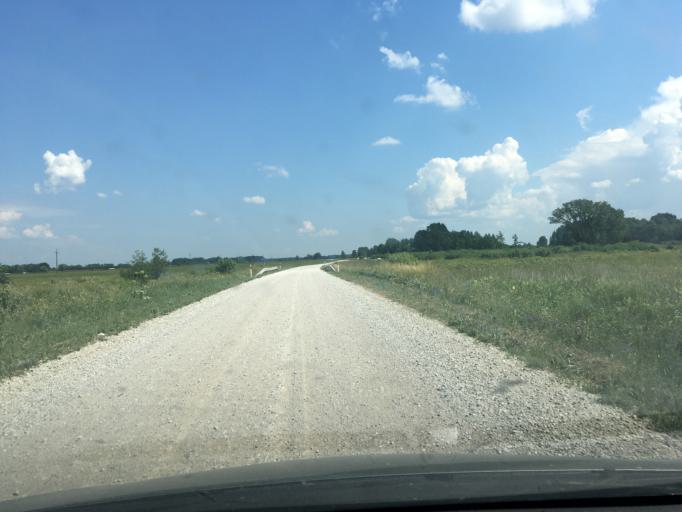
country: EE
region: Laeaene
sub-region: Lihula vald
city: Lihula
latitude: 58.7112
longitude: 24.0450
